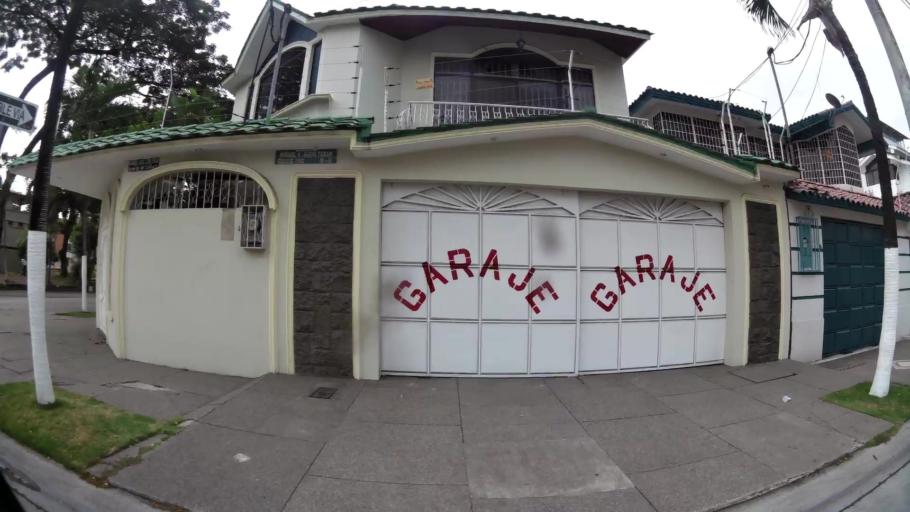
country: EC
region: Guayas
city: Eloy Alfaro
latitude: -2.1475
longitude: -79.8919
